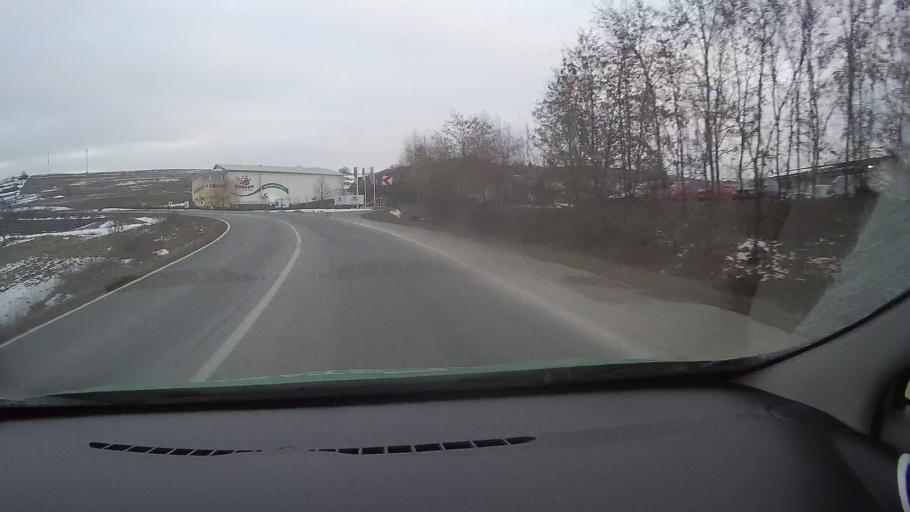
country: RO
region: Harghita
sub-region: Comuna Lupeni
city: Lupeni
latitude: 46.3558
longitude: 25.2397
